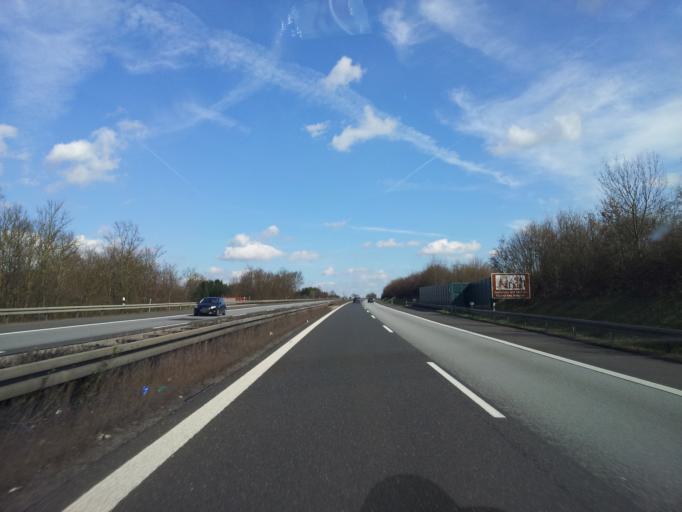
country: DE
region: Bavaria
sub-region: Regierungsbezirk Unterfranken
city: Gochsheim
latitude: 50.0307
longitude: 10.2839
